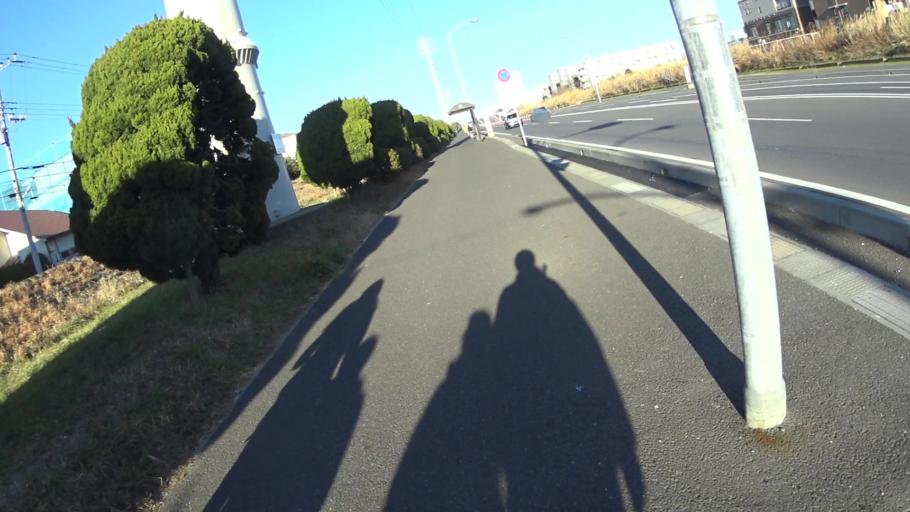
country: JP
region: Tokyo
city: Urayasu
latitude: 35.6404
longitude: 139.9104
